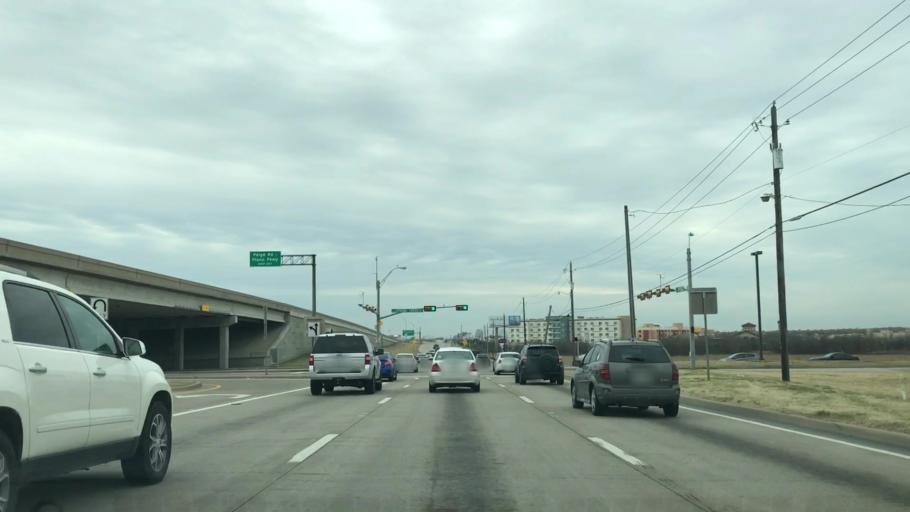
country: US
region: Texas
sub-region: Denton County
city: The Colony
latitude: 33.0832
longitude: -96.8517
